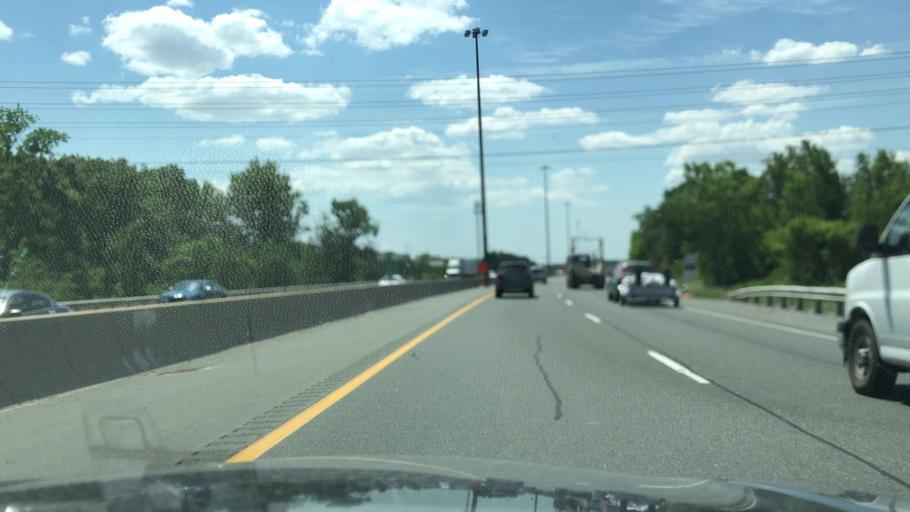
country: CA
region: Ontario
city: Niagara Falls
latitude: 43.0792
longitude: -79.1187
